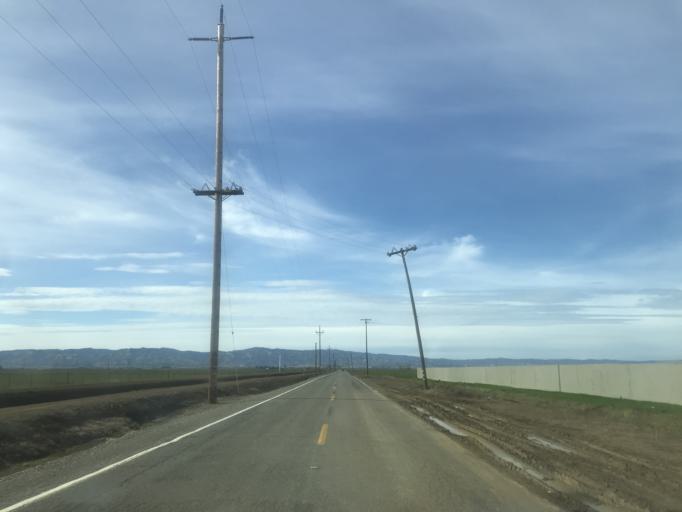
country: US
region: California
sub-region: Yolo County
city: Cottonwood
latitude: 38.6636
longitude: -121.9085
